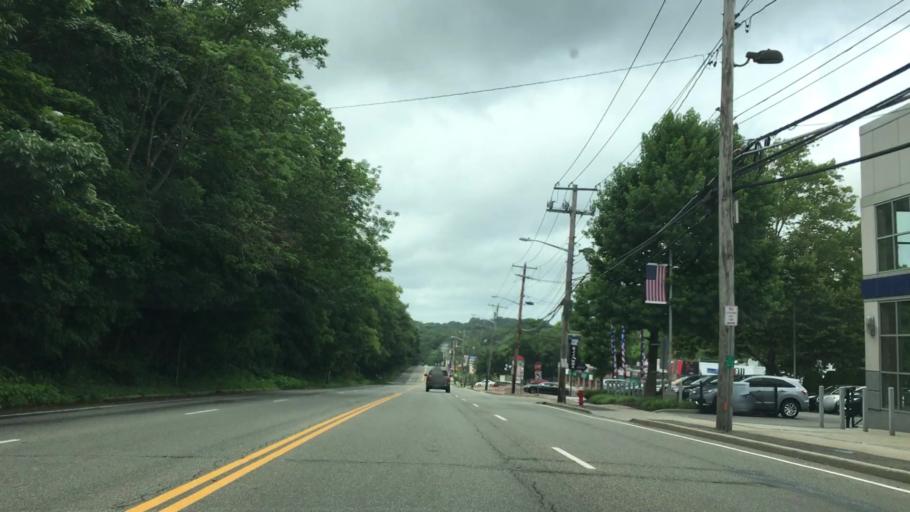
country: US
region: New York
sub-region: Suffolk County
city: West Hills
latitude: 40.8282
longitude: -73.4313
